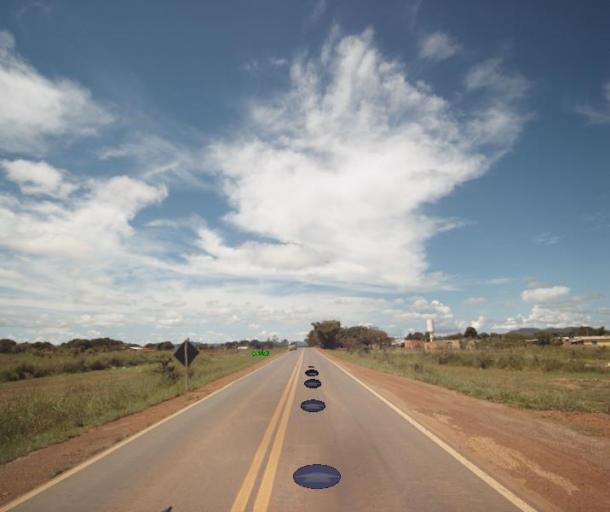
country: BR
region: Goias
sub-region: Padre Bernardo
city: Padre Bernardo
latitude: -15.3571
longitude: -48.2284
